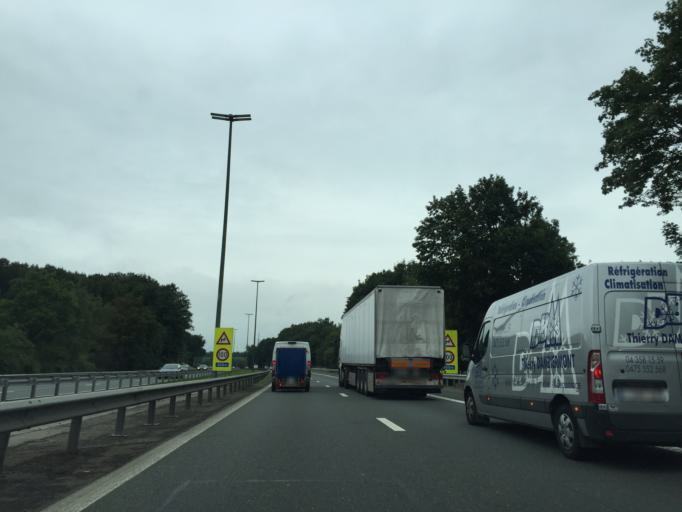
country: BE
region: Wallonia
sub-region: Province de Liege
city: Dison
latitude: 50.6202
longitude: 5.8535
